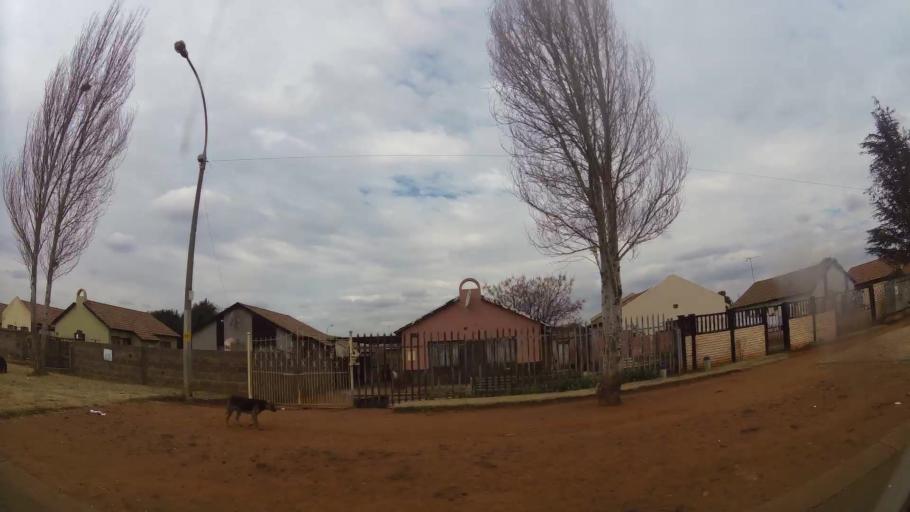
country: ZA
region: Gauteng
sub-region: Ekurhuleni Metropolitan Municipality
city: Germiston
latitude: -26.3863
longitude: 28.1238
